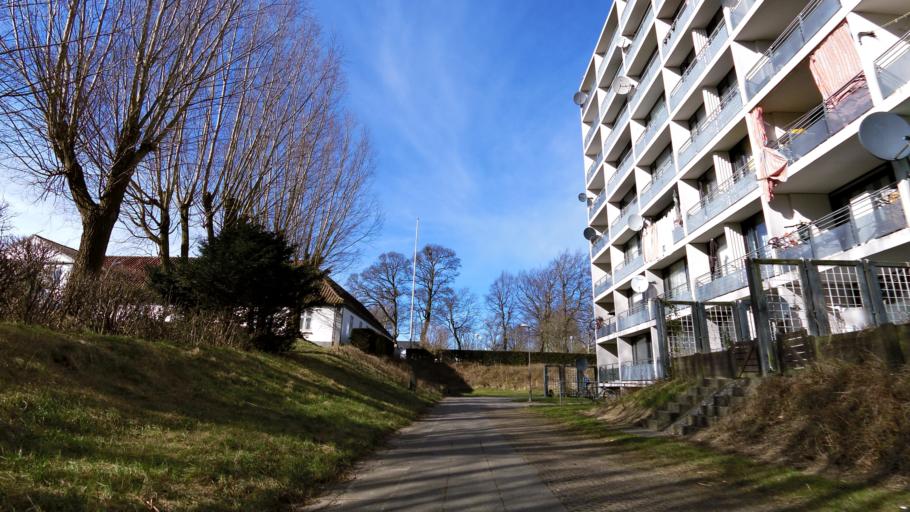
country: DK
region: Central Jutland
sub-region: Arhus Kommune
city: Stavtrup
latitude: 56.1618
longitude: 10.1394
